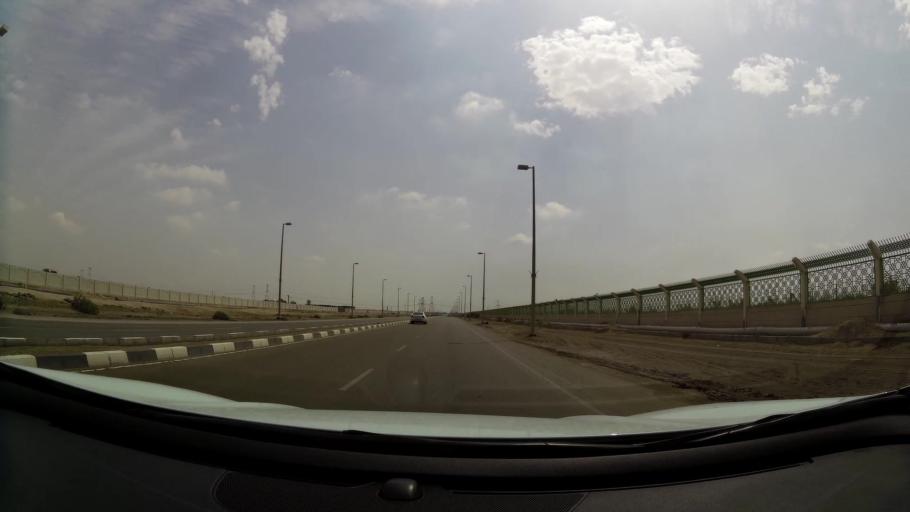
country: AE
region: Abu Dhabi
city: Abu Dhabi
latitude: 24.5326
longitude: 54.6358
